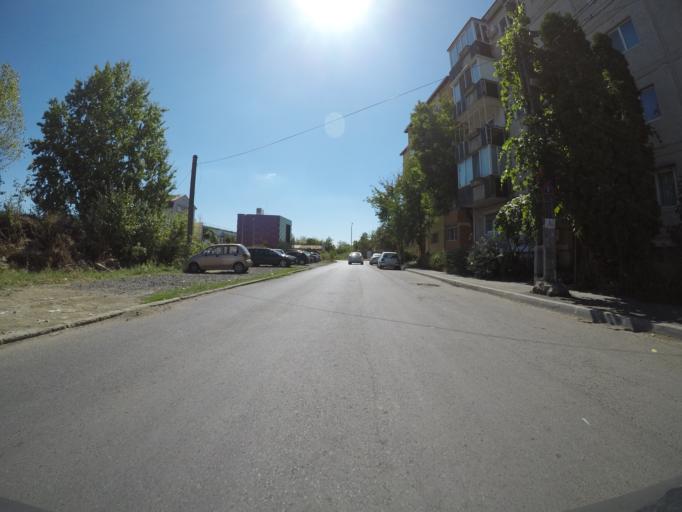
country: RO
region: Timis
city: Timisoara
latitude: 45.7452
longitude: 21.2512
